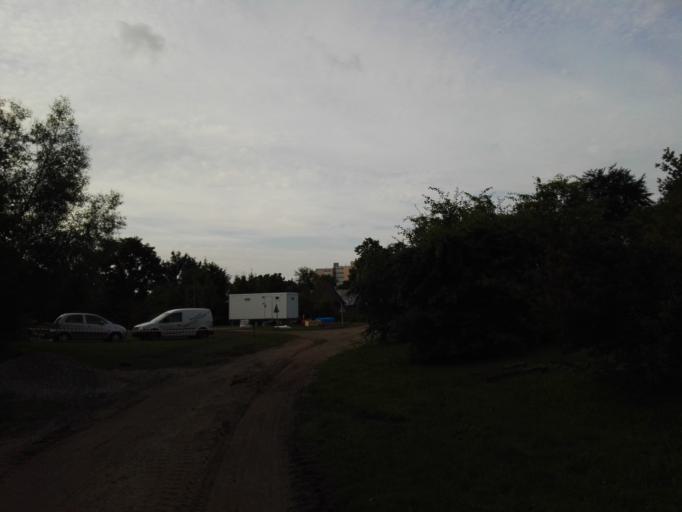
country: DK
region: Capital Region
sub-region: Ballerup Kommune
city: Malov
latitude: 55.7528
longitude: 12.3149
